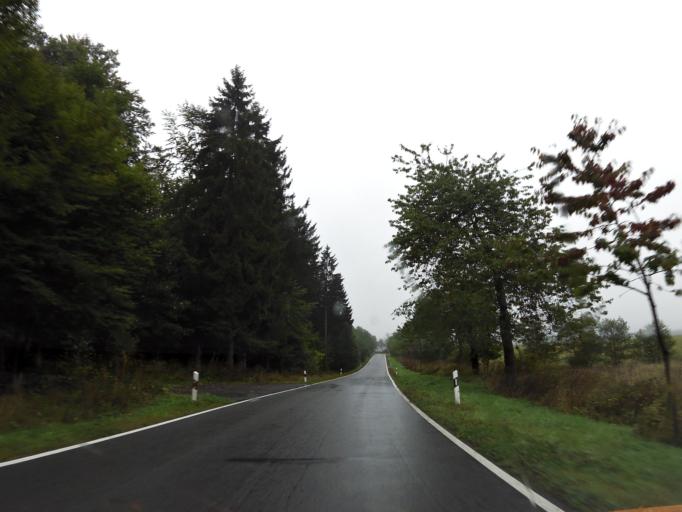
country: DE
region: Saxony-Anhalt
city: Hasselfelde
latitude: 51.6551
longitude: 10.8660
